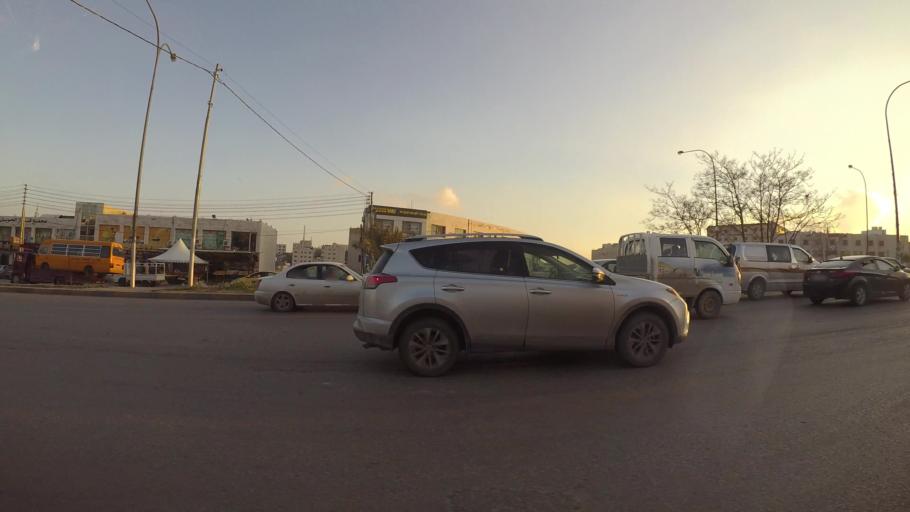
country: JO
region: Amman
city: Al Quwaysimah
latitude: 31.9004
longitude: 35.9337
